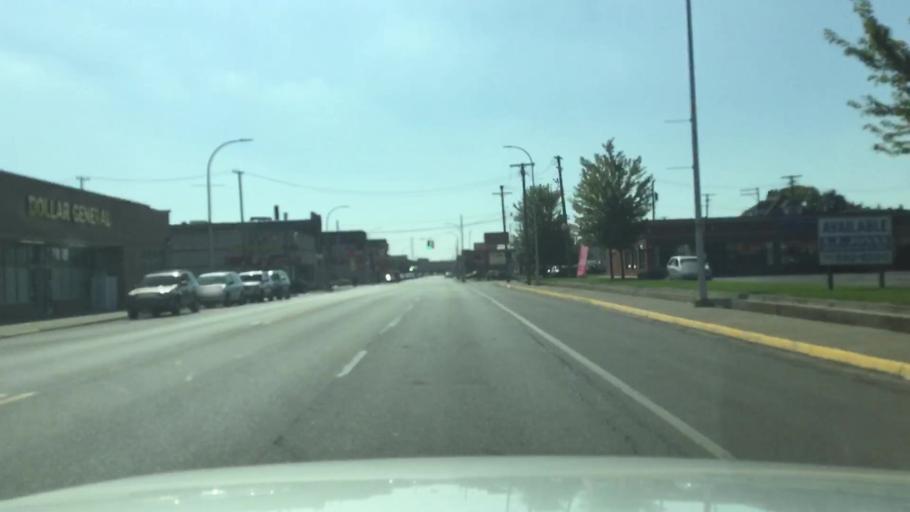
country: US
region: Michigan
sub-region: Wayne County
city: Hamtramck
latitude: 42.3925
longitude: -83.0550
